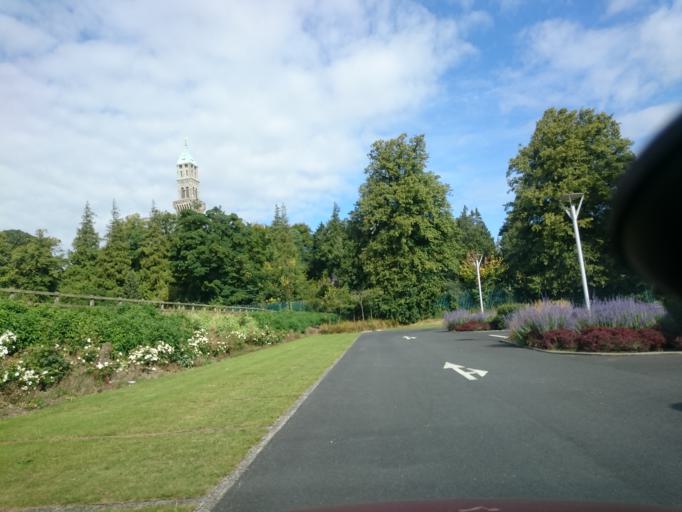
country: IE
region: Leinster
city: Castleknock
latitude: 53.3627
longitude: -6.3612
